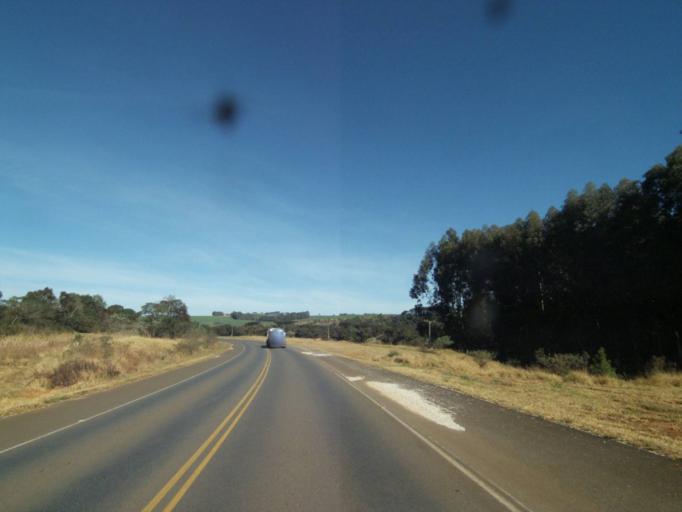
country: BR
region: Parana
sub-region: Tibagi
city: Tibagi
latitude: -24.4747
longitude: -50.4459
